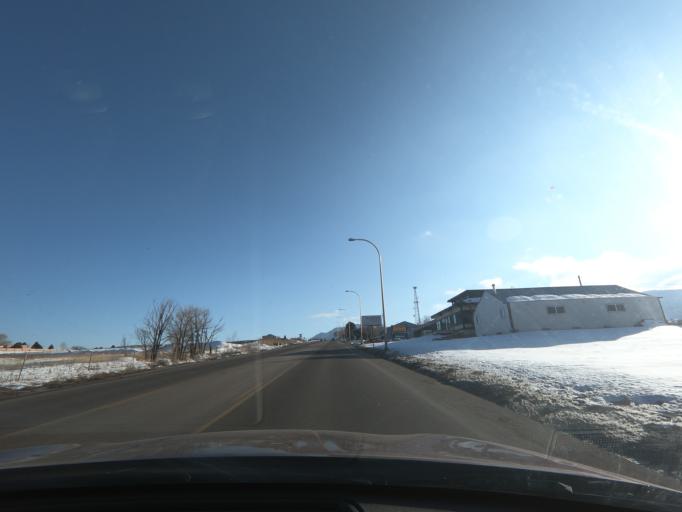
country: US
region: Colorado
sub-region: El Paso County
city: Colorado Springs
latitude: 38.8350
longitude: -104.8592
